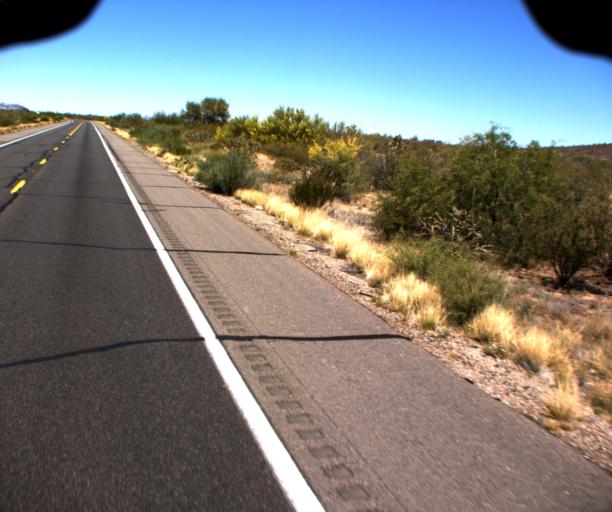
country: US
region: Arizona
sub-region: Yavapai County
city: Congress
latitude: 34.1713
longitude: -113.0195
